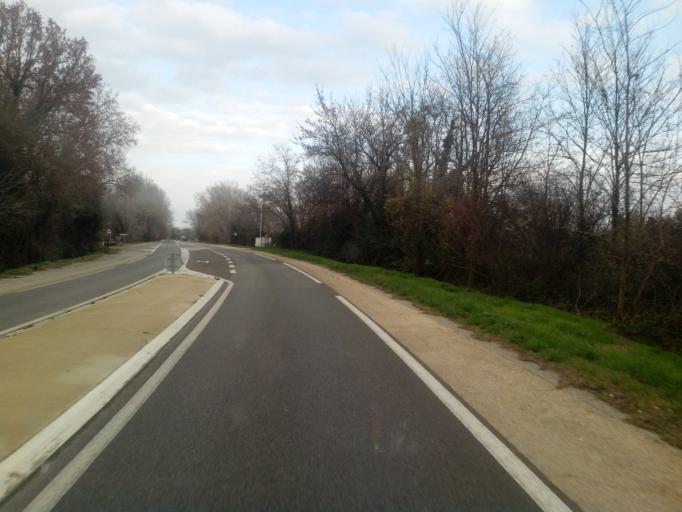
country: FR
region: Provence-Alpes-Cote d'Azur
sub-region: Departement des Bouches-du-Rhone
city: Saintes-Maries-de-la-Mer
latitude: 43.5549
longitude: 4.4123
